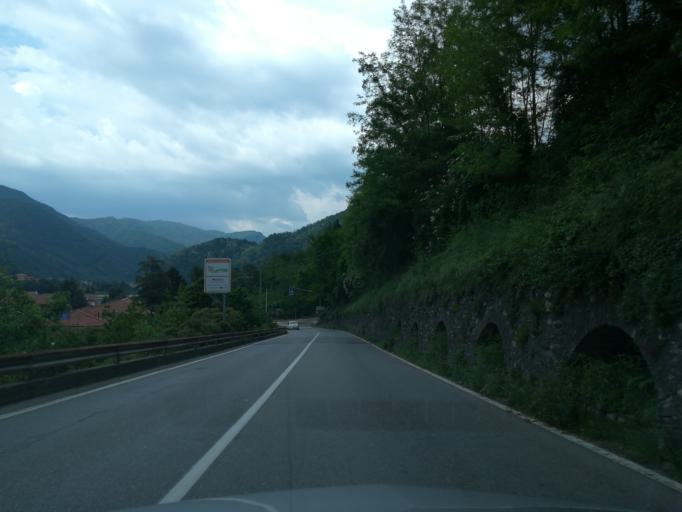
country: IT
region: Lombardy
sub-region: Provincia di Bergamo
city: Alme
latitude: 45.7446
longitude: 9.6091
